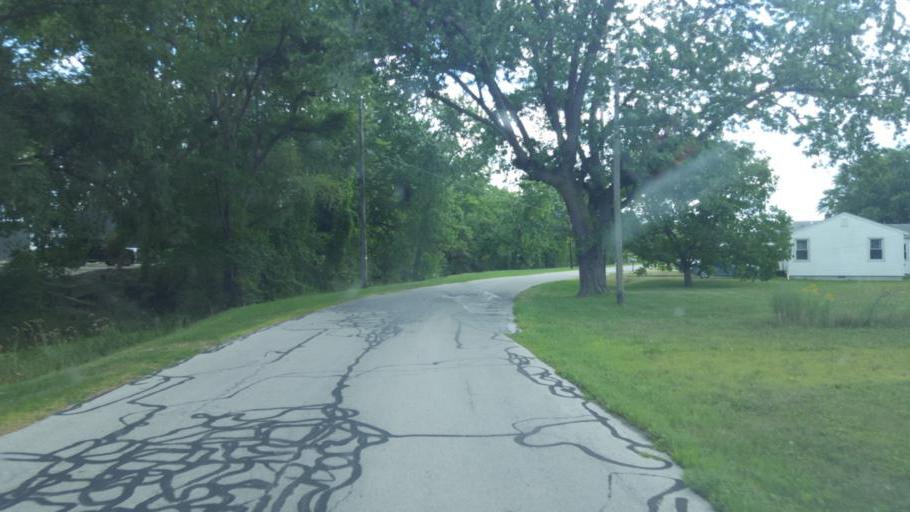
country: US
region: Ohio
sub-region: Lucas County
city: Curtice
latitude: 41.6590
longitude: -83.2540
